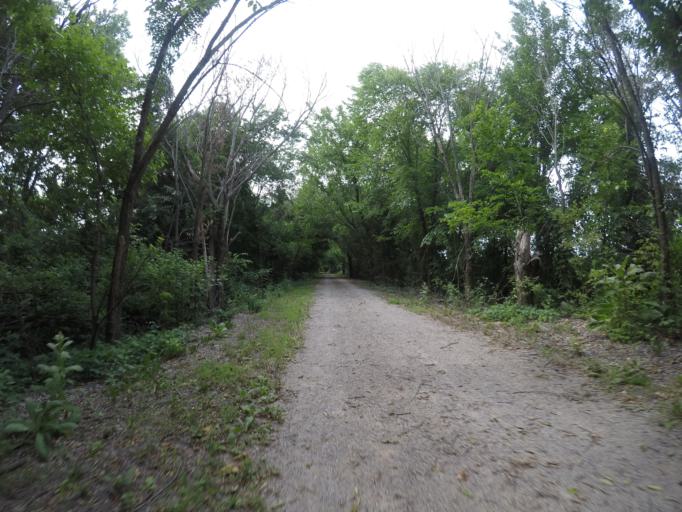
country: US
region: Kansas
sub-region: Anderson County
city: Garnett
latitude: 38.4108
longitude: -95.2614
